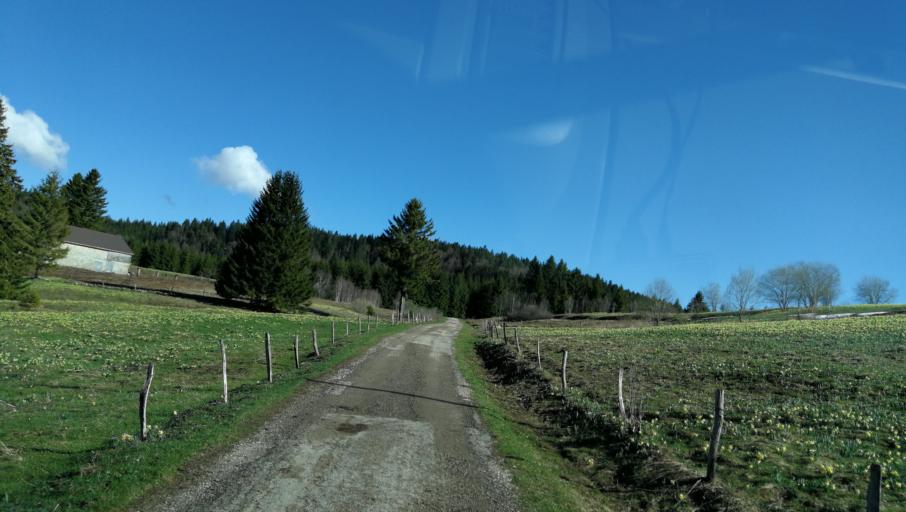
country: FR
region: Franche-Comte
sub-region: Departement du Jura
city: Saint-Claude
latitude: 46.3007
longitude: 5.8621
